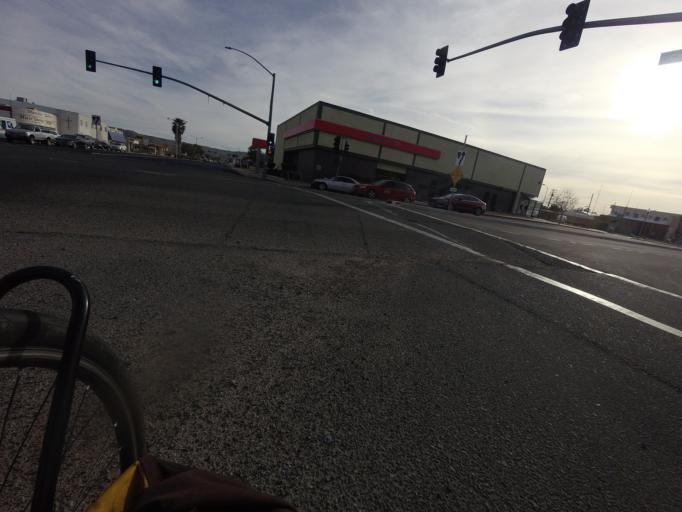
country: US
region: California
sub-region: Kern County
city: Ridgecrest
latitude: 35.6226
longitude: -117.6701
